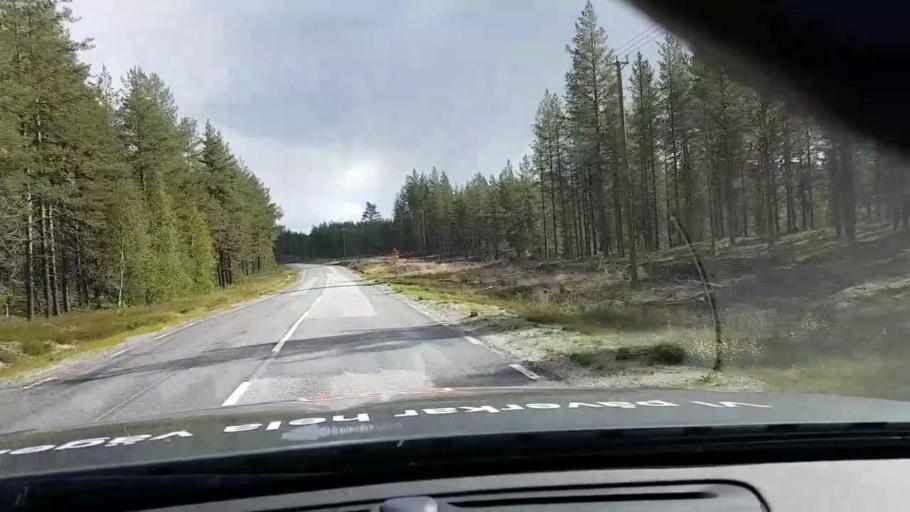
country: SE
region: Vaesterbotten
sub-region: Asele Kommun
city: Asele
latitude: 63.8555
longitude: 17.3877
